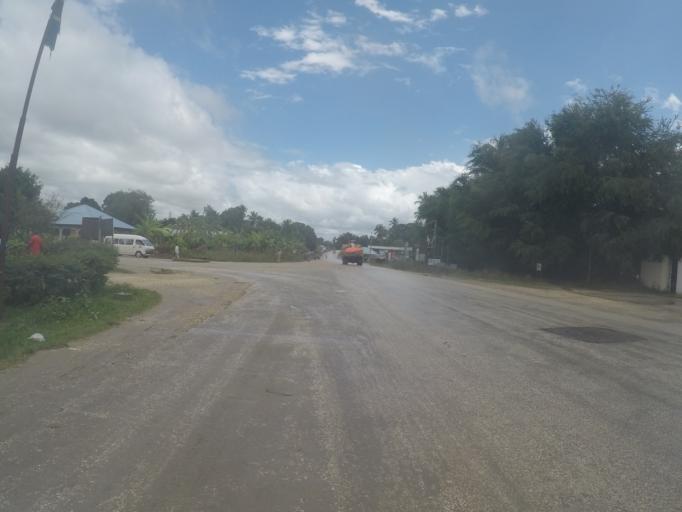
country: TZ
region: Zanzibar North
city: Gamba
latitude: -5.9894
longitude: 39.2518
